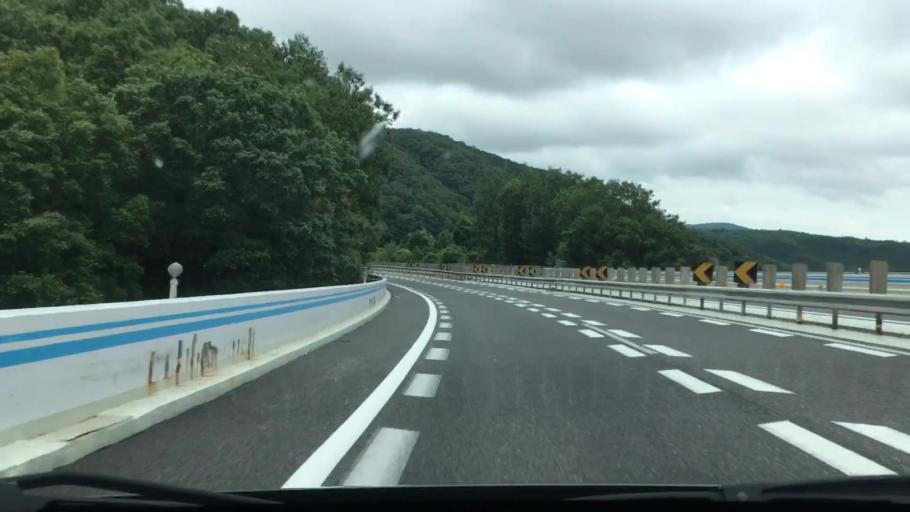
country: JP
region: Hiroshima
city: Miyoshi
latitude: 34.7832
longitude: 132.8443
